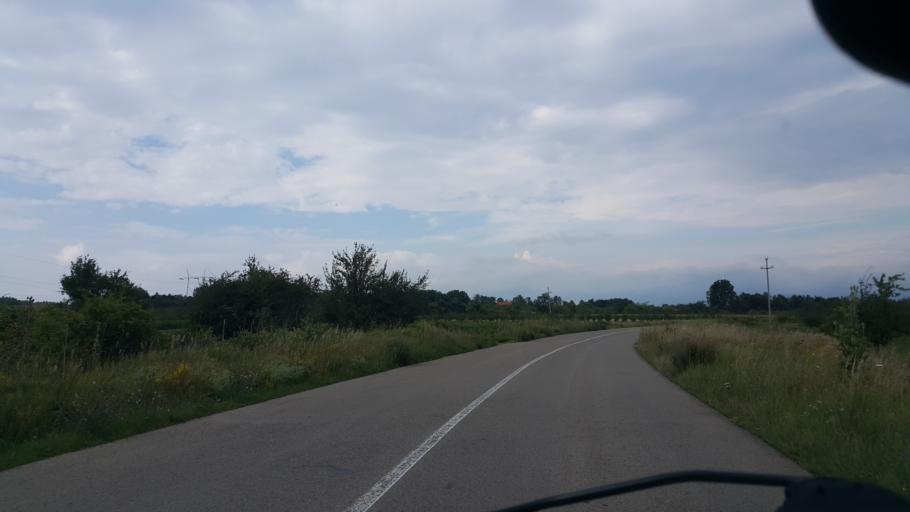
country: RS
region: Central Serbia
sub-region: Toplicki Okrug
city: Blace
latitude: 43.2491
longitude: 21.2600
